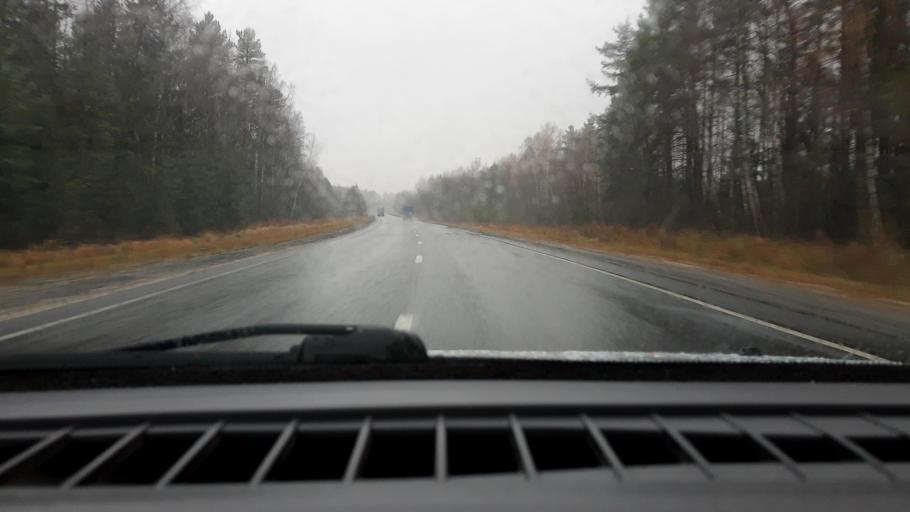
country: RU
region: Nizjnij Novgorod
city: Linda
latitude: 56.6651
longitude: 44.1328
